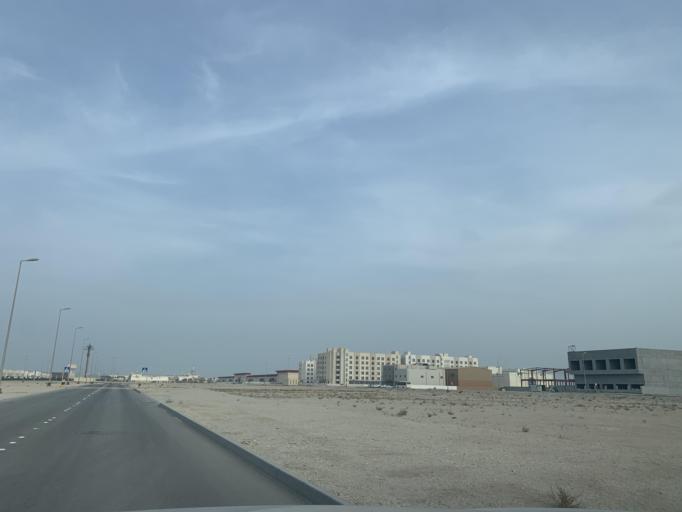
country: BH
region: Muharraq
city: Al Muharraq
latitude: 26.3113
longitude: 50.6193
